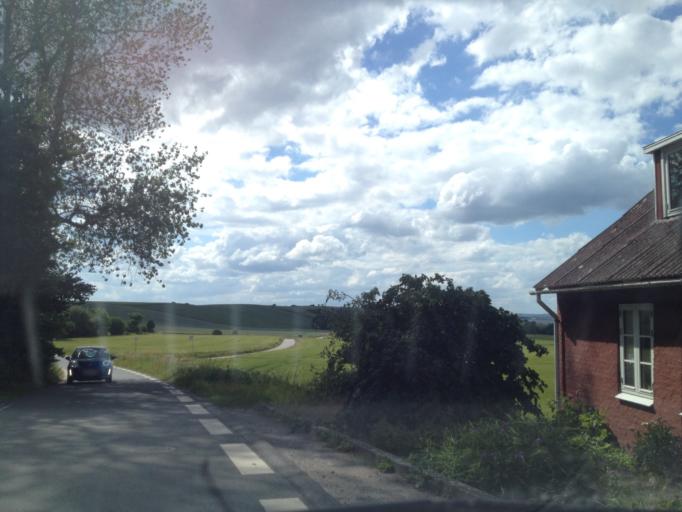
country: DK
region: Central Jutland
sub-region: Syddjurs Kommune
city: Ronde
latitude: 56.1962
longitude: 10.5068
